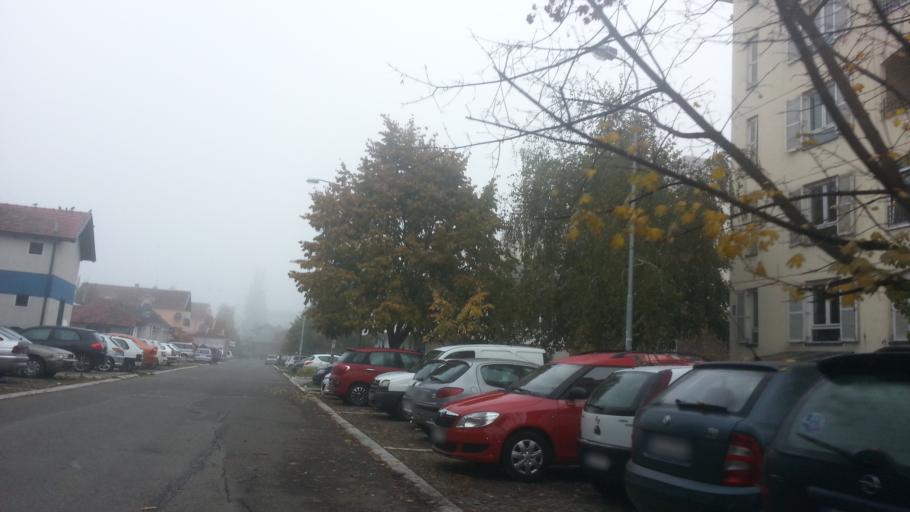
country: RS
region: Central Serbia
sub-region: Belgrade
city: Zemun
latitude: 44.8343
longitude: 20.4105
